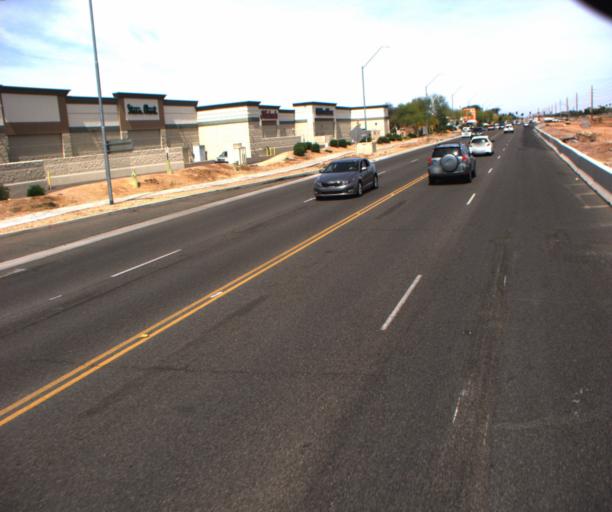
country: US
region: Arizona
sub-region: Maricopa County
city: Surprise
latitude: 33.6400
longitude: -112.3521
